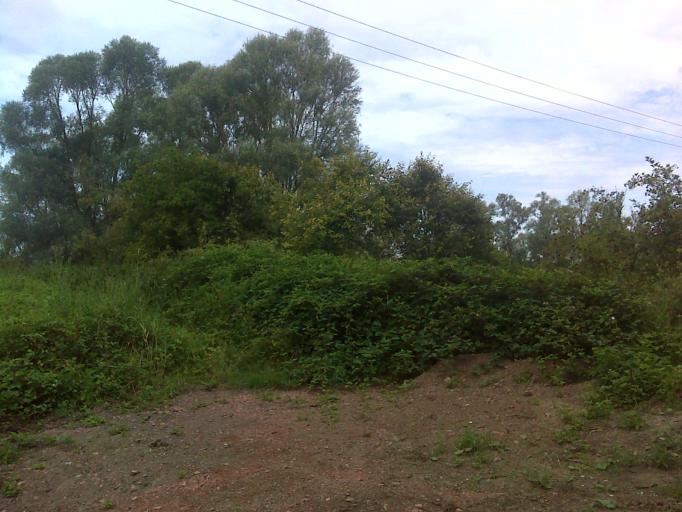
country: BE
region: Wallonia
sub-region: Province du Hainaut
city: Bernissart
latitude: 50.4489
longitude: 3.6264
